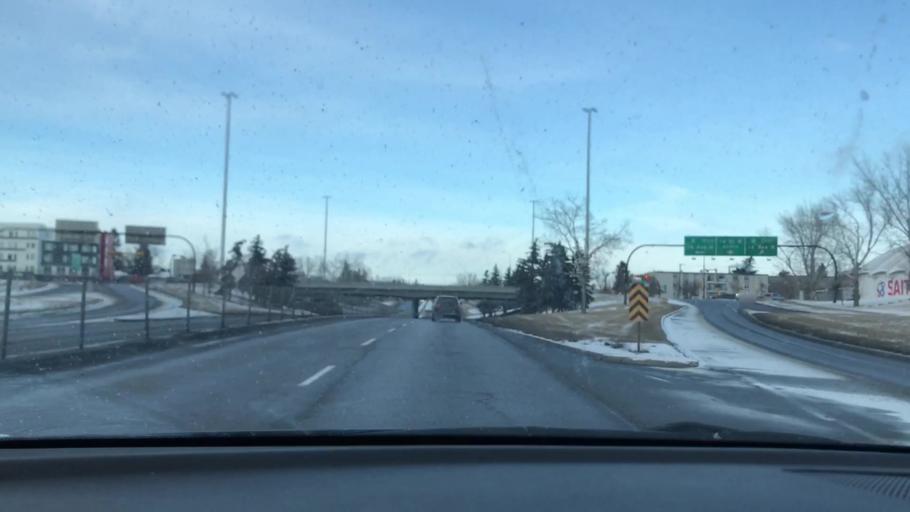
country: CA
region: Alberta
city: Calgary
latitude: 51.0653
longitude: -114.0946
